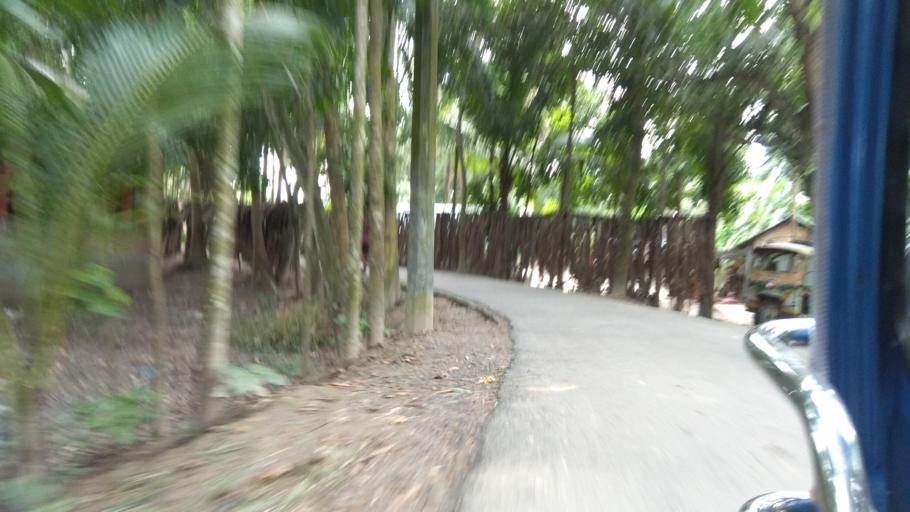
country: BD
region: Khulna
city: Kalia
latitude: 23.0311
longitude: 89.6466
